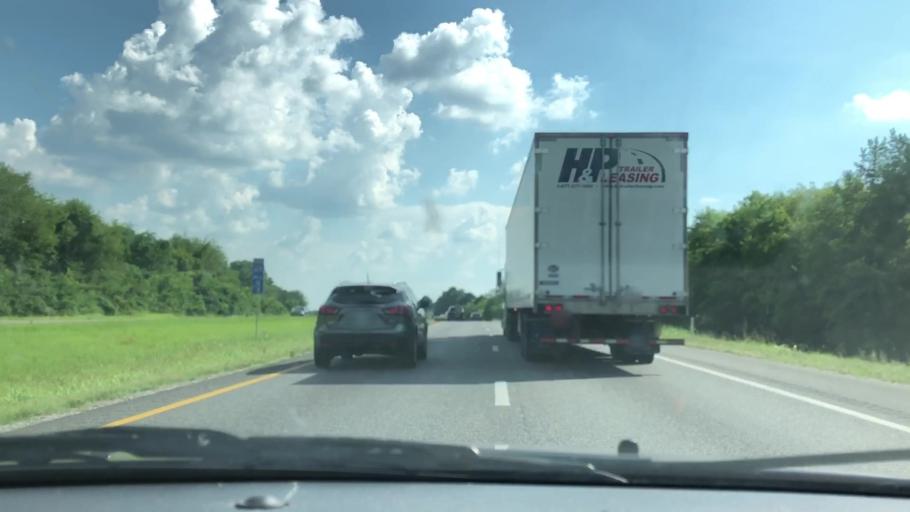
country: US
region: Tennessee
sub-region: Williamson County
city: Thompson's Station
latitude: 35.7956
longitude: -86.8586
